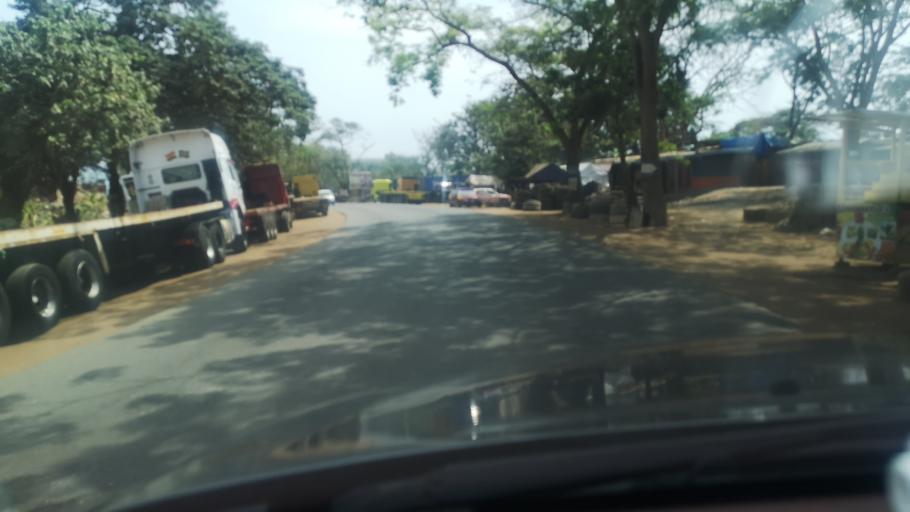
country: GH
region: Greater Accra
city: Tema
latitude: 5.6231
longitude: -0.0213
